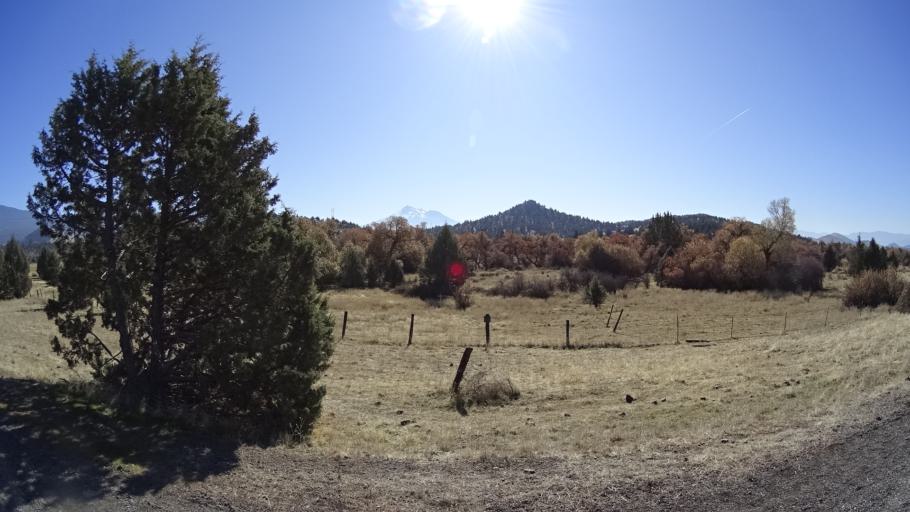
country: US
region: California
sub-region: Siskiyou County
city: Montague
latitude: 41.7285
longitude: -122.3641
